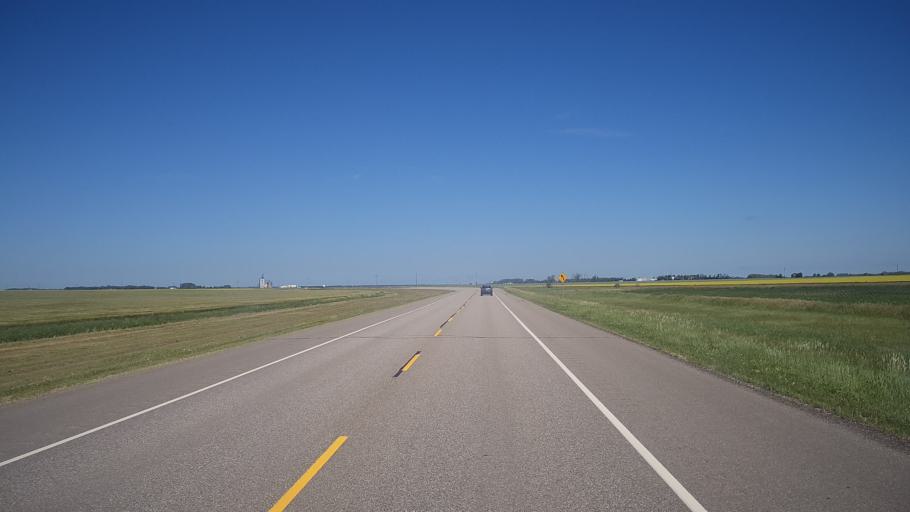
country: CA
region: Manitoba
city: Portage la Prairie
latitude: 50.0574
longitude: -98.4731
